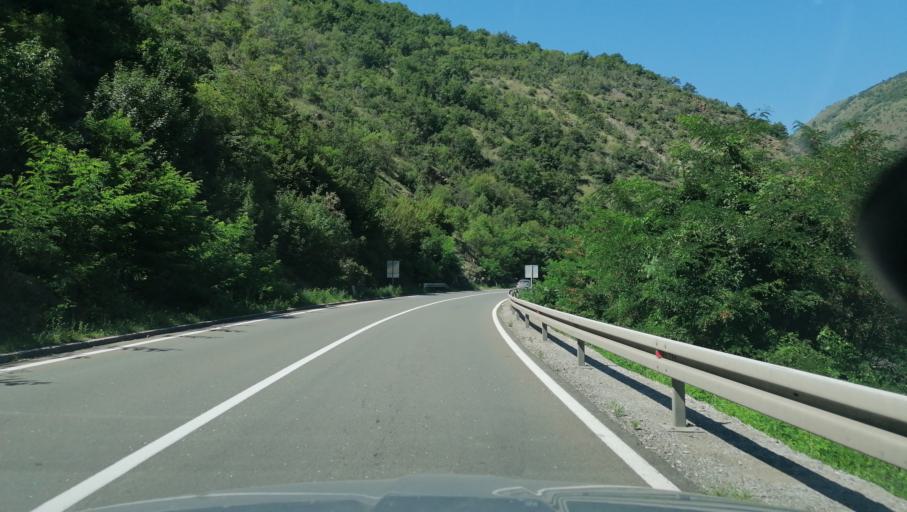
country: RS
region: Central Serbia
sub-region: Raski Okrug
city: Kraljevo
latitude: 43.5976
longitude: 20.5575
